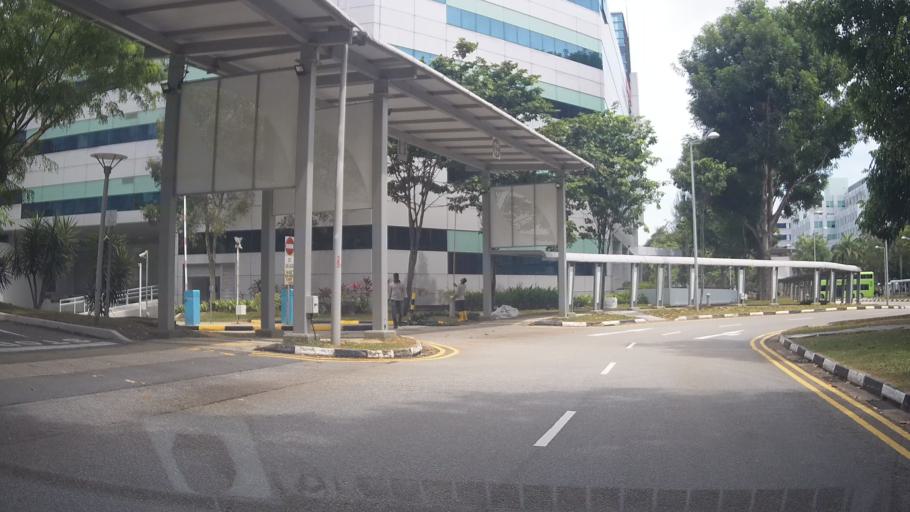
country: SG
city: Singapore
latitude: 1.3369
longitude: 103.9647
